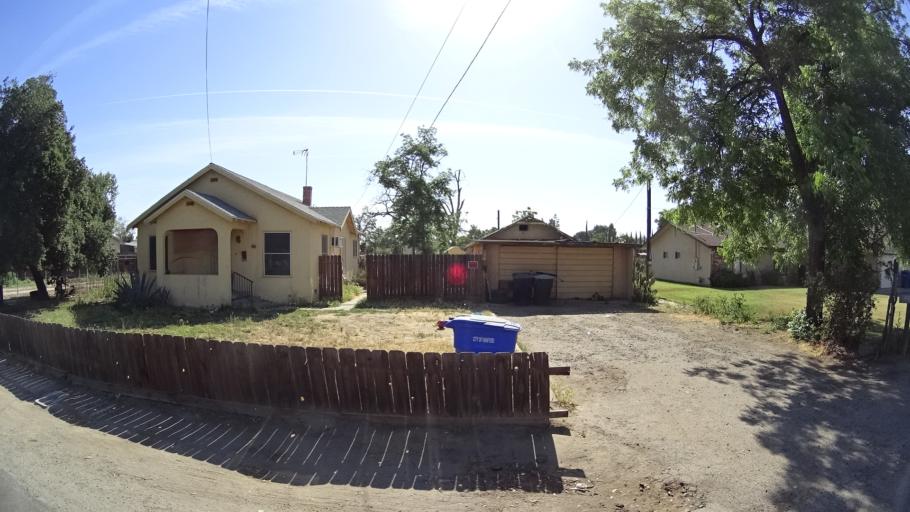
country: US
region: California
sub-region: Kings County
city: Hanford
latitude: 36.3419
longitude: -119.6350
